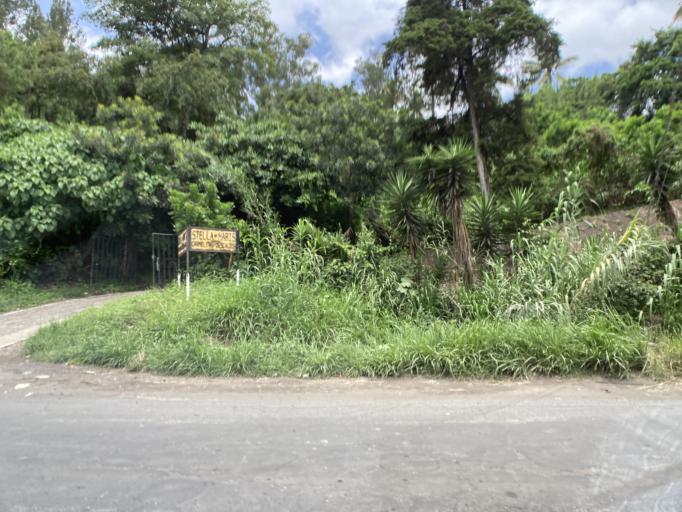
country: GT
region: Guatemala
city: Villa Canales
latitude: 14.4575
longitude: -90.5750
